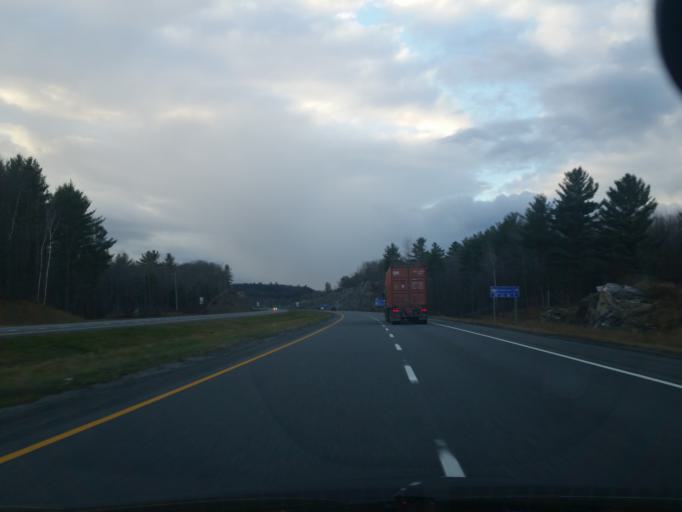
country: CA
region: Quebec
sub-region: Outaouais
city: Papineauville
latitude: 45.6722
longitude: -74.9222
